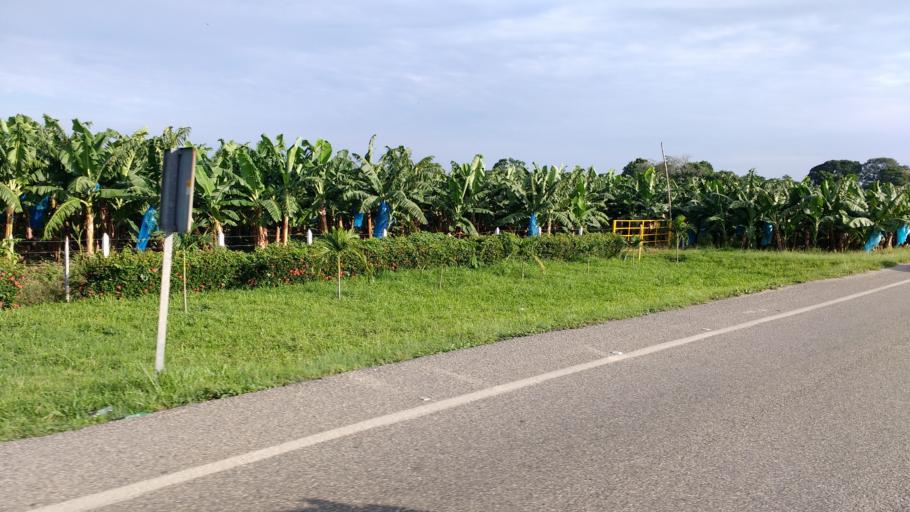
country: MX
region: Tabasco
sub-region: Teapa
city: Eureka y Belen
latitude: 17.6210
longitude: -92.9629
